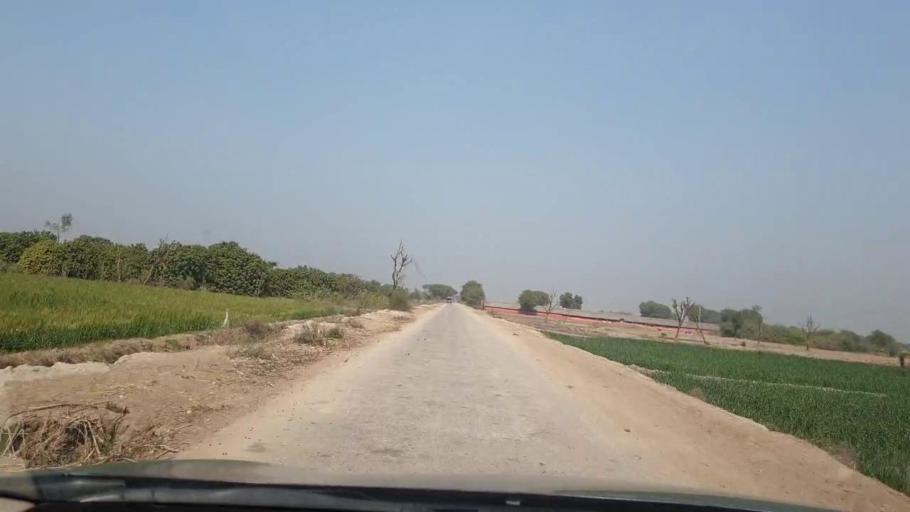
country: PK
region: Sindh
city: Tando Allahyar
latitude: 25.4947
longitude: 68.7959
